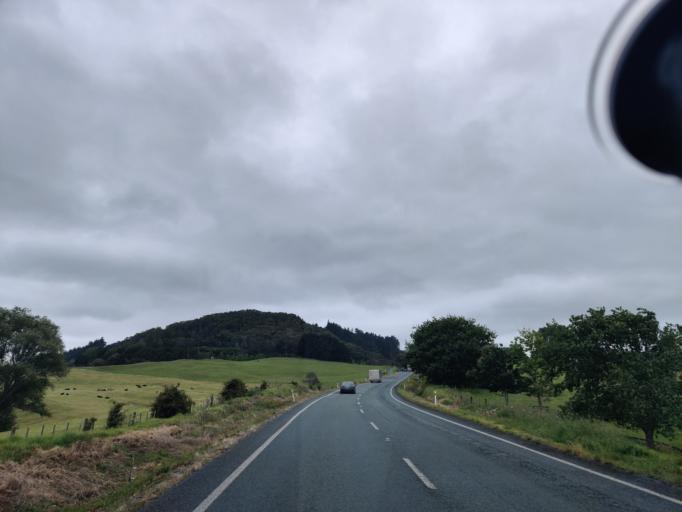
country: NZ
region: Northland
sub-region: Whangarei
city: Ruakaka
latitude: -36.0982
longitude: 174.4234
